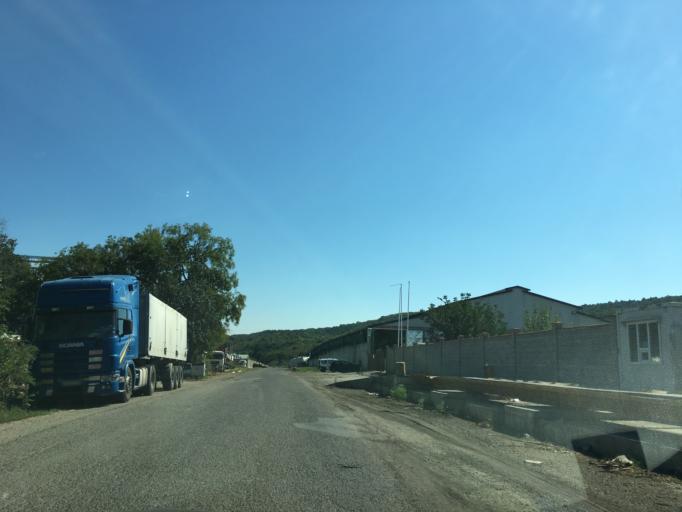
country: RO
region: Dolj
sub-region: Comuna Desa
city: Desa
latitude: 43.7657
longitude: 23.0154
